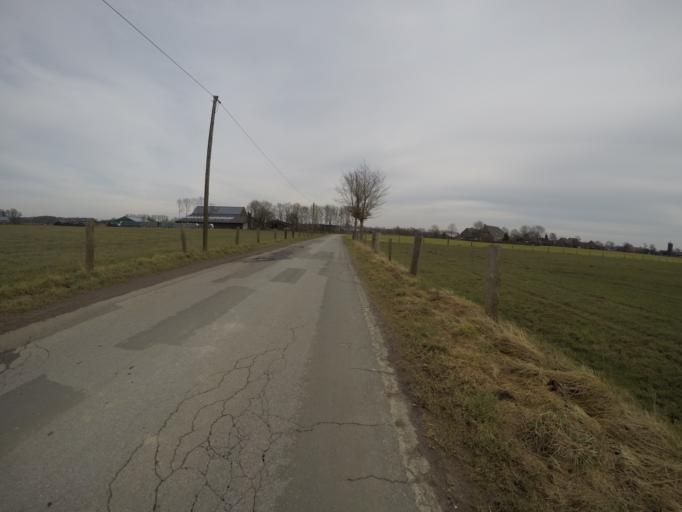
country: DE
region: North Rhine-Westphalia
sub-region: Regierungsbezirk Dusseldorf
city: Hamminkeln
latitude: 51.7610
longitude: 6.5737
